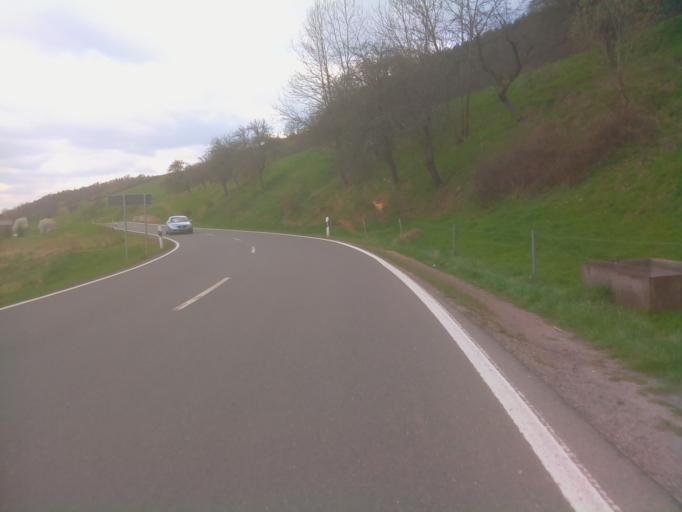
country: DE
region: Thuringia
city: Weissbach
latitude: 50.8312
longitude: 11.7893
